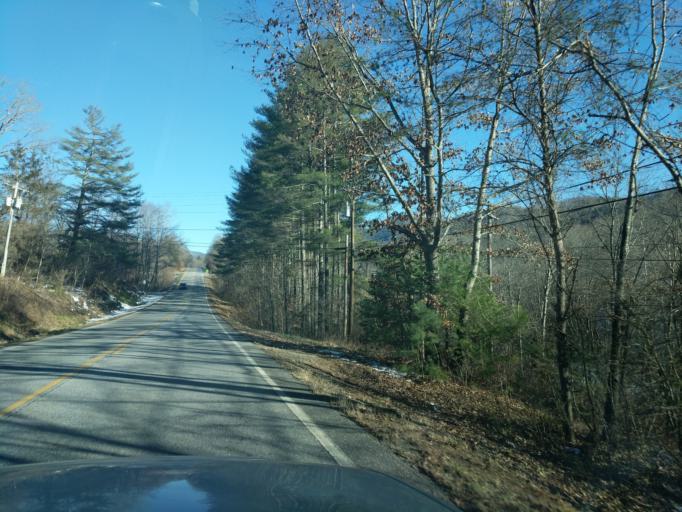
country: US
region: Georgia
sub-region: Towns County
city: Hiawassee
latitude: 34.9254
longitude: -83.6855
